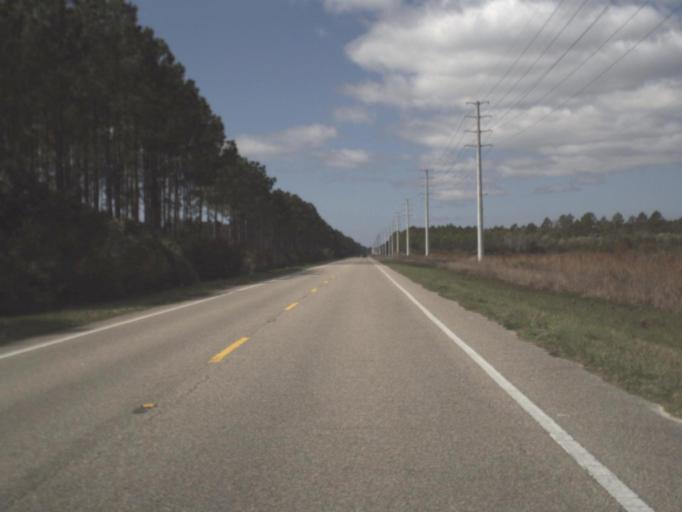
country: US
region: Florida
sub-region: Franklin County
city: Apalachicola
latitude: 29.7245
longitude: -85.0920
